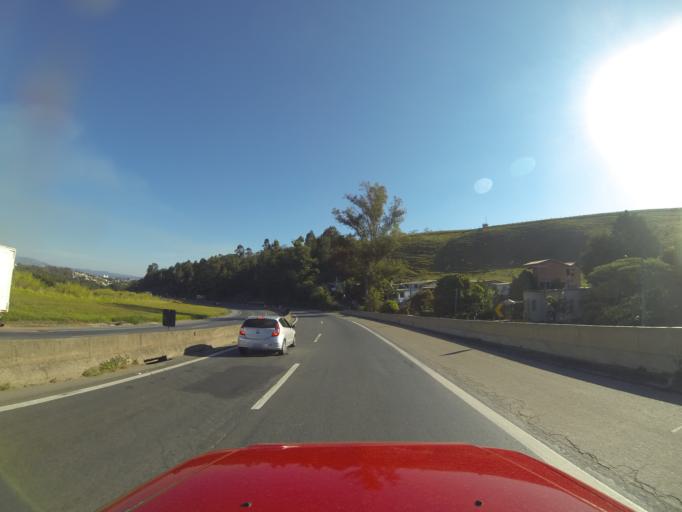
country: BR
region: Sao Paulo
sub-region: Atibaia
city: Atibaia
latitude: -23.0776
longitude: -46.5689
